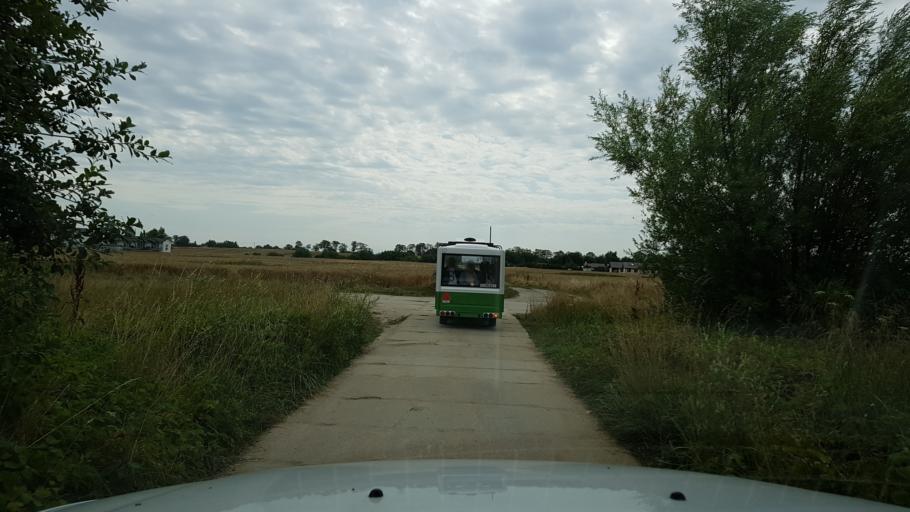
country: PL
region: West Pomeranian Voivodeship
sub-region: Powiat koszalinski
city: Mielno
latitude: 54.2434
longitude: 15.9348
